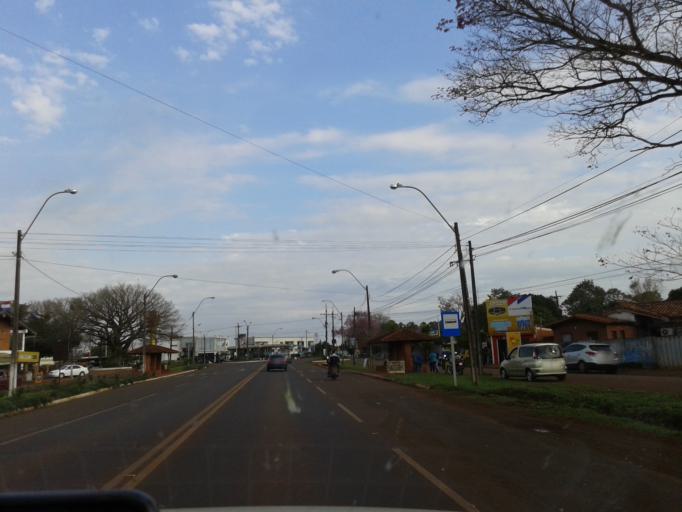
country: PY
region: Itapua
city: Bella Vista
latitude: -27.0417
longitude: -55.5785
